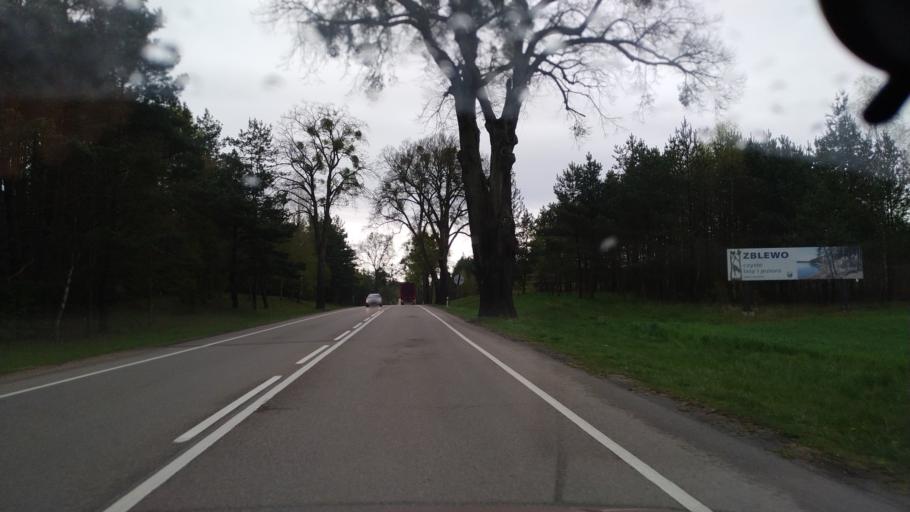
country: PL
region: Pomeranian Voivodeship
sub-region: Powiat starogardzki
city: Kaliska
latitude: 53.9093
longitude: 18.2604
